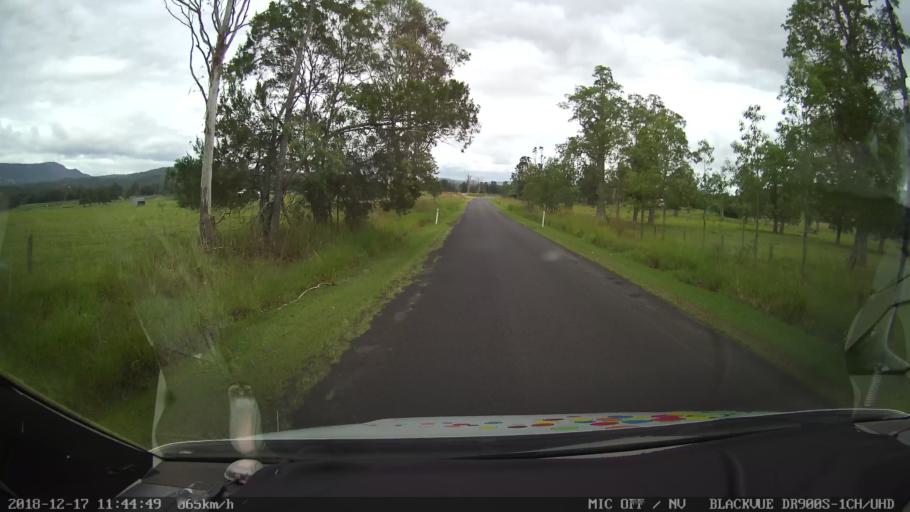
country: AU
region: New South Wales
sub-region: Kyogle
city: Kyogle
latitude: -28.6497
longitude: 152.5951
